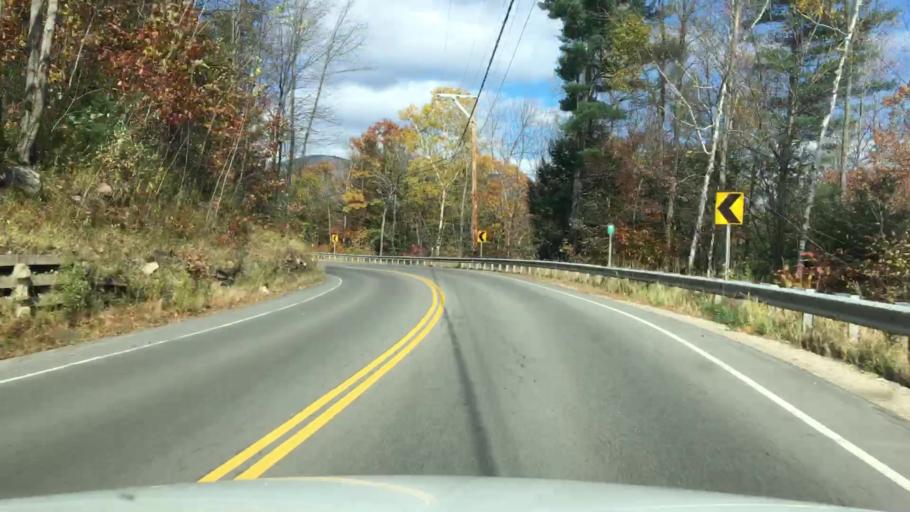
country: US
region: New Hampshire
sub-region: Coos County
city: Gorham
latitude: 44.3772
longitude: -71.1726
